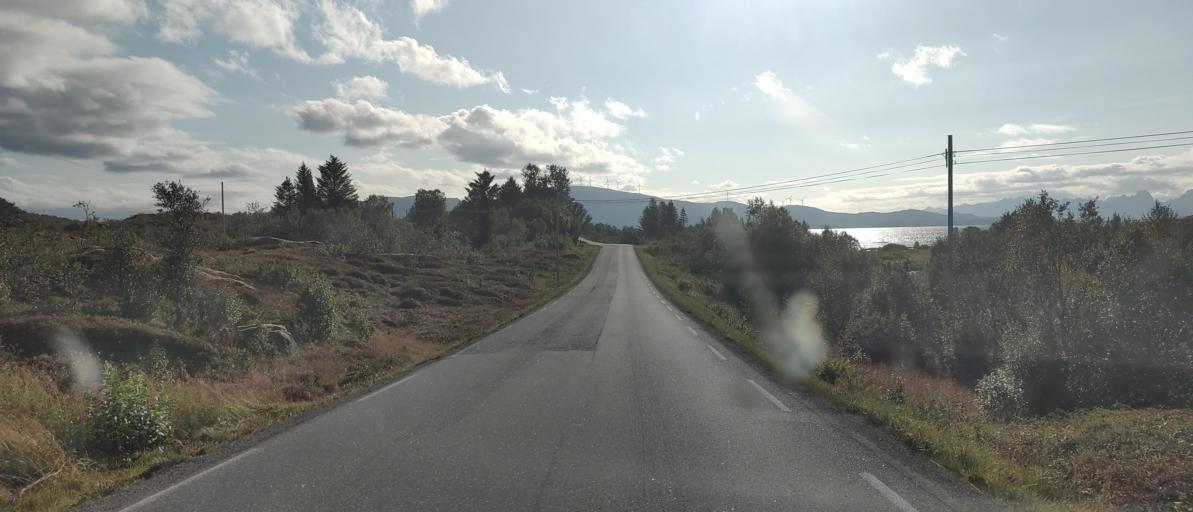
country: NO
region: Nordland
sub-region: Sortland
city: Sortland
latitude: 68.7728
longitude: 15.4772
